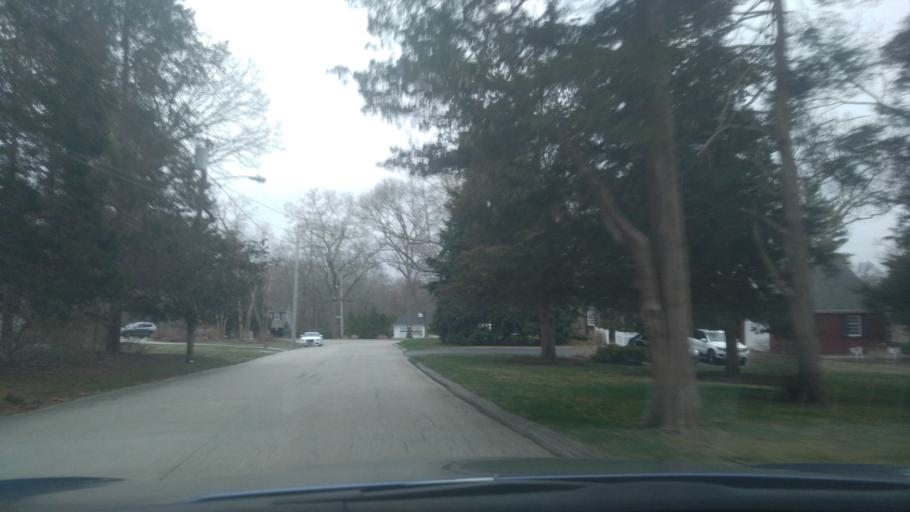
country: US
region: Rhode Island
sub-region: Kent County
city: East Greenwich
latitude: 41.6686
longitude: -71.4621
